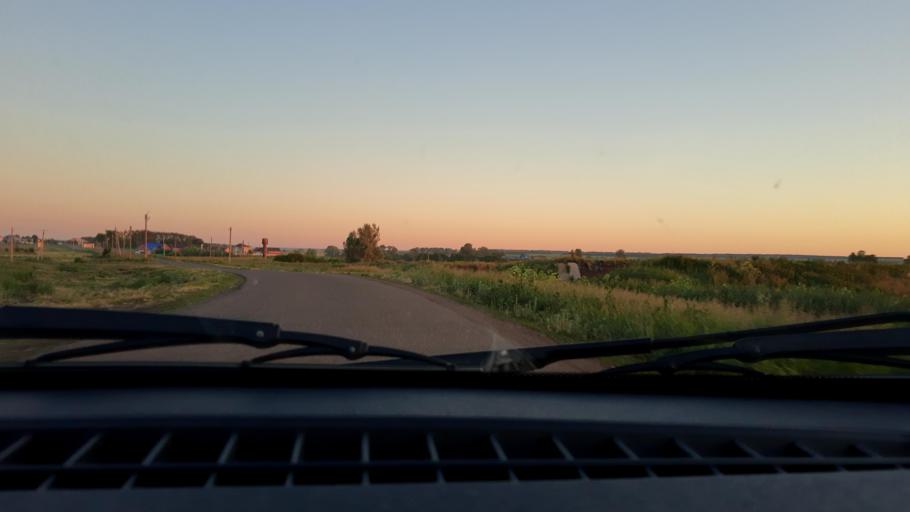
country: RU
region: Bashkortostan
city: Asanovo
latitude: 54.8984
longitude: 55.6271
